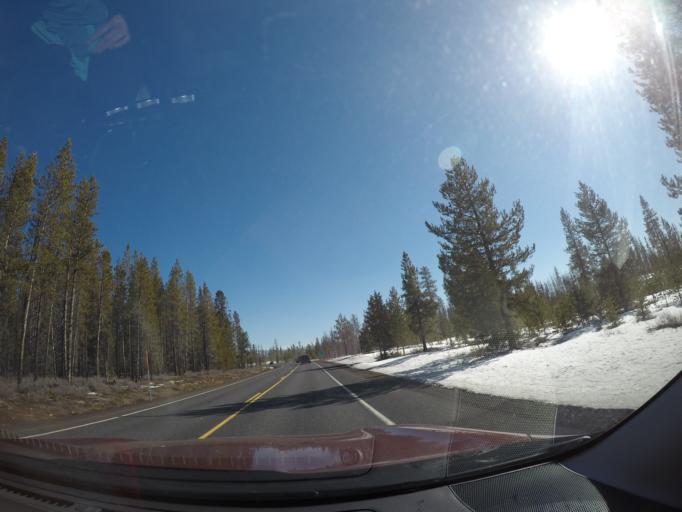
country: US
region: Oregon
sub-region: Deschutes County
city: Three Rivers
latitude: 43.8578
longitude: -121.5238
